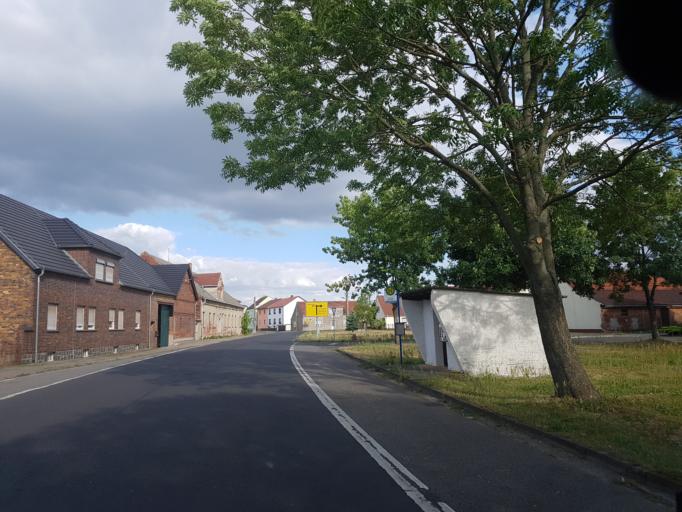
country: DE
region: Brandenburg
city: Herzberg
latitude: 51.7475
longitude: 13.2897
